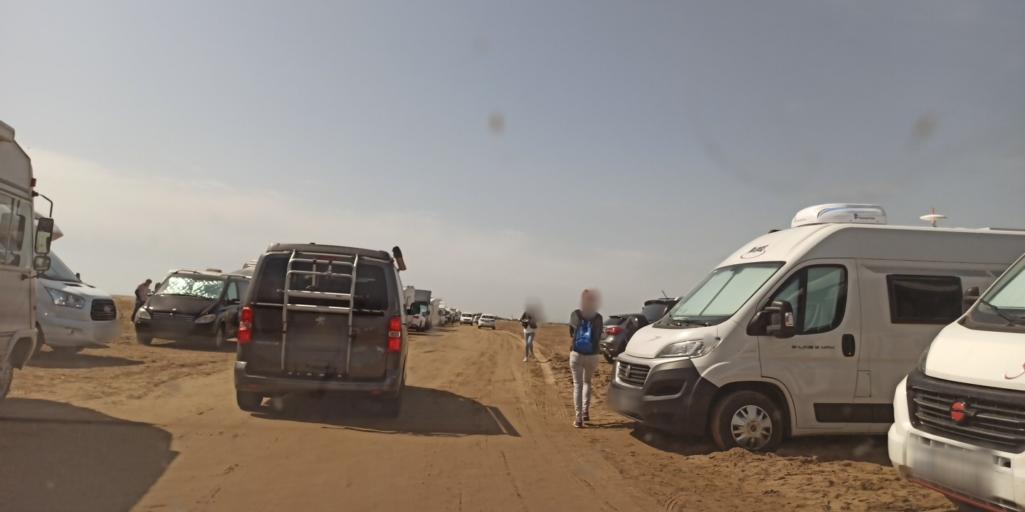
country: ES
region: Catalonia
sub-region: Provincia de Tarragona
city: Deltebre
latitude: 40.6351
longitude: 0.7480
